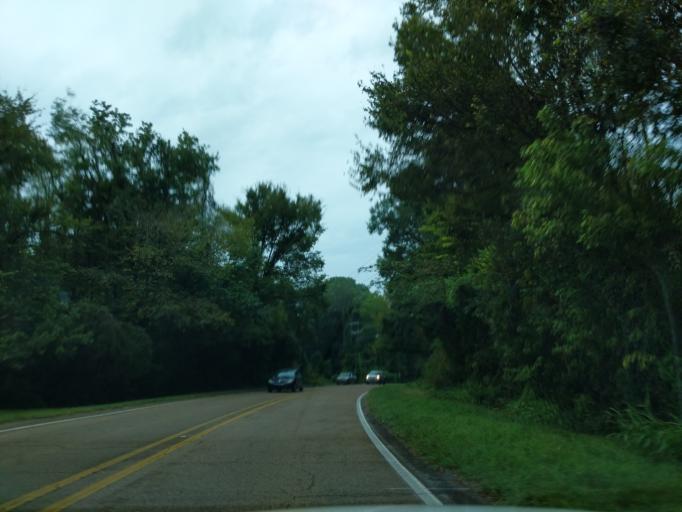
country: US
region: Mississippi
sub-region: Warren County
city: Vicksburg
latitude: 32.3166
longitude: -90.8839
